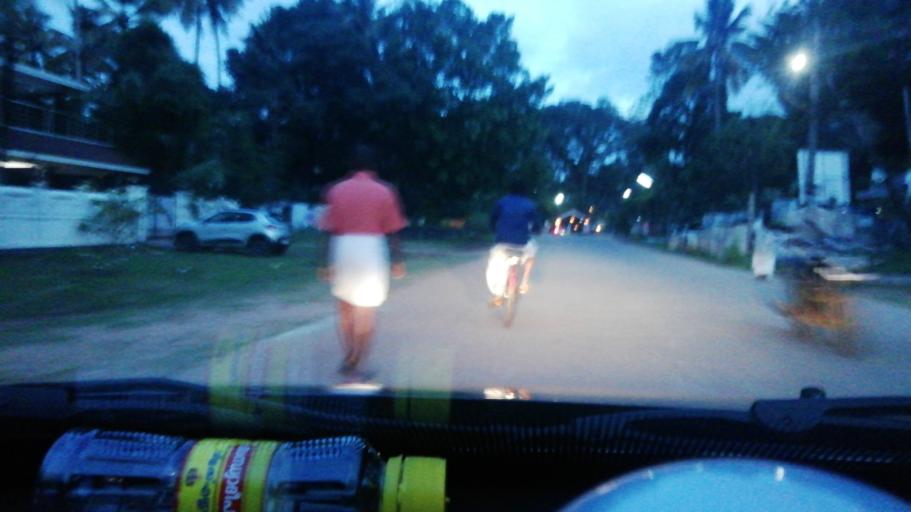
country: IN
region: Kerala
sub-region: Thiruvananthapuram
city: Paravur
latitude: 8.8124
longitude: 76.6667
